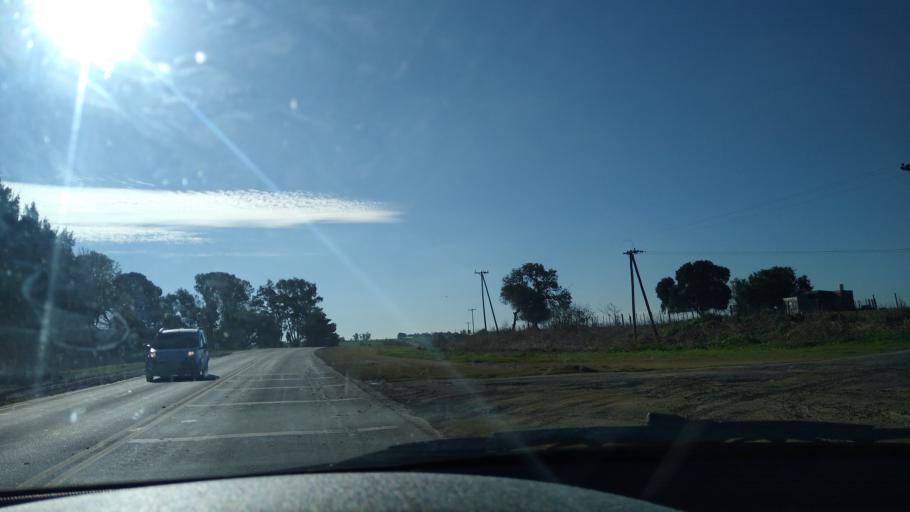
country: AR
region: Entre Rios
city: Aranguren
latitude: -32.4112
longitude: -60.3214
